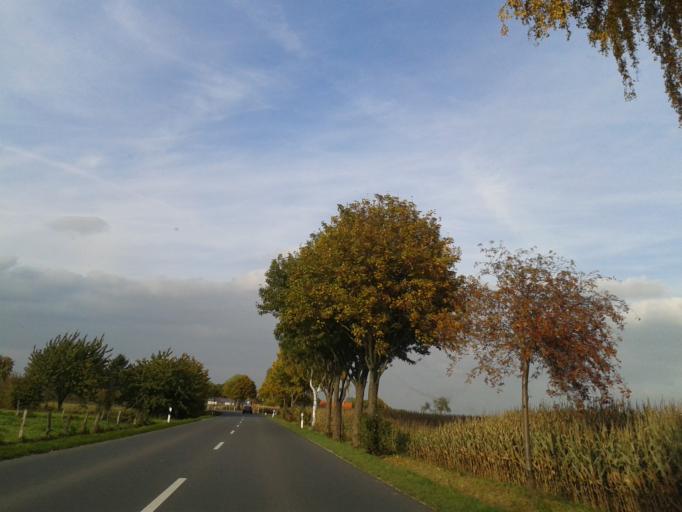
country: DE
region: North Rhine-Westphalia
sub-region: Regierungsbezirk Detmold
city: Salzkotten
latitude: 51.7299
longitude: 8.6635
